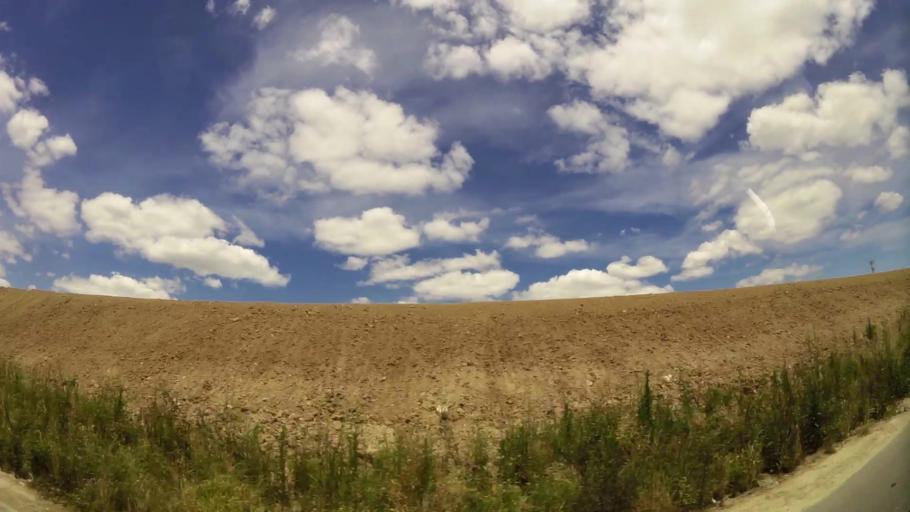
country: UY
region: Montevideo
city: Pajas Blancas
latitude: -34.8524
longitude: -56.2721
